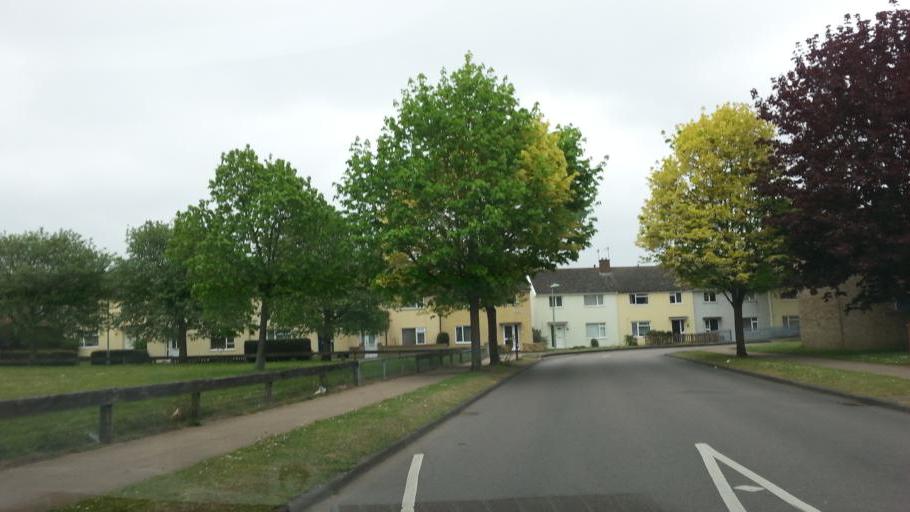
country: GB
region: England
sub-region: Suffolk
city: Bury St Edmunds
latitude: 52.2568
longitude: 0.6985
